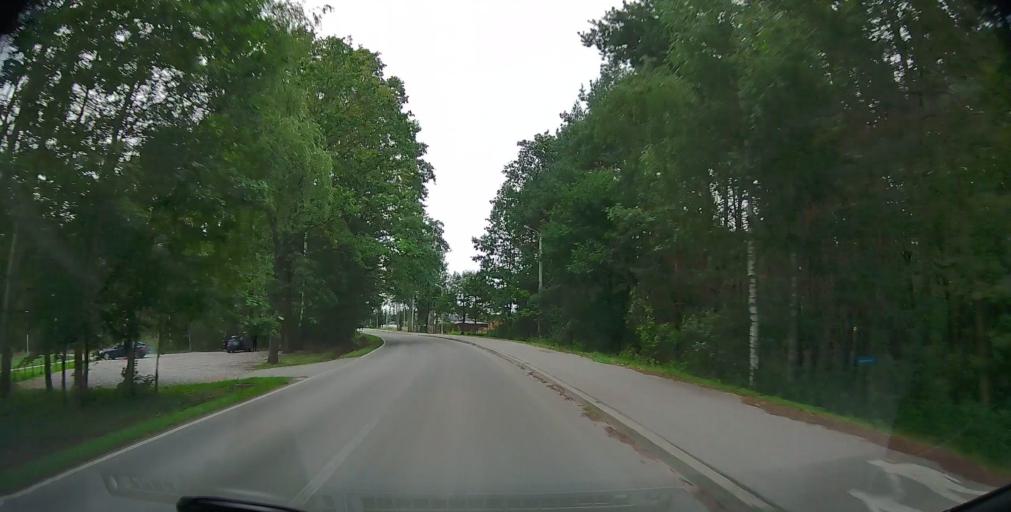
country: PL
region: Masovian Voivodeship
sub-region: Powiat radomski
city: Zakrzew
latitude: 51.4287
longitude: 21.0584
